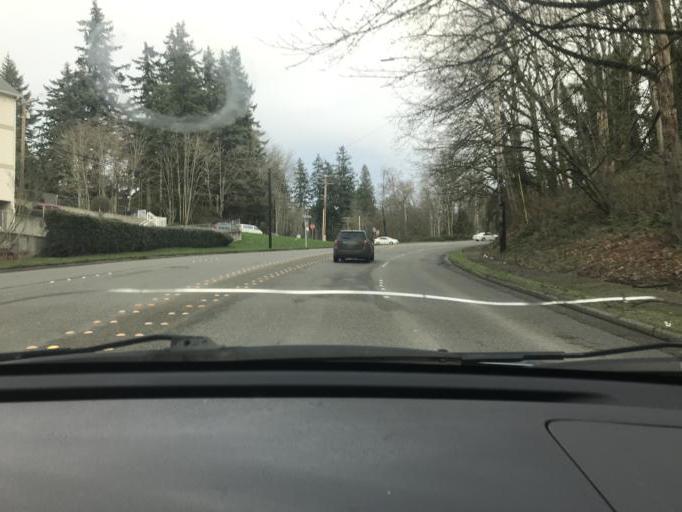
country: US
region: Washington
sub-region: Snohomish County
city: Alderwood Manor
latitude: 47.8487
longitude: -122.2888
